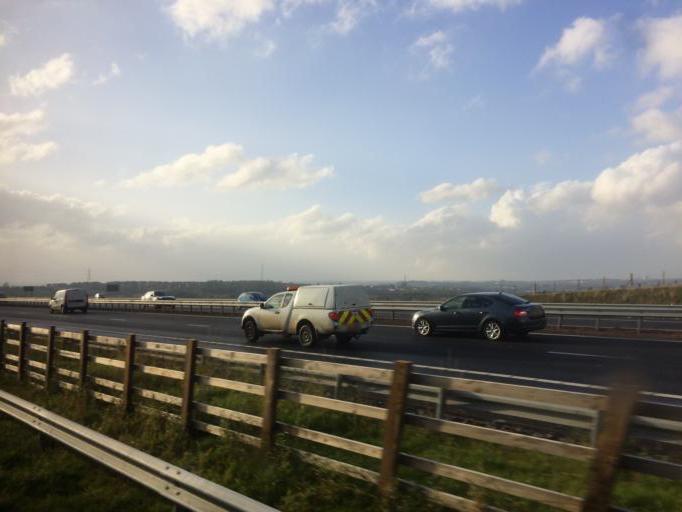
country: GB
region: Scotland
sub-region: North Lanarkshire
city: Newarthill
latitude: 55.8372
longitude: -3.9222
